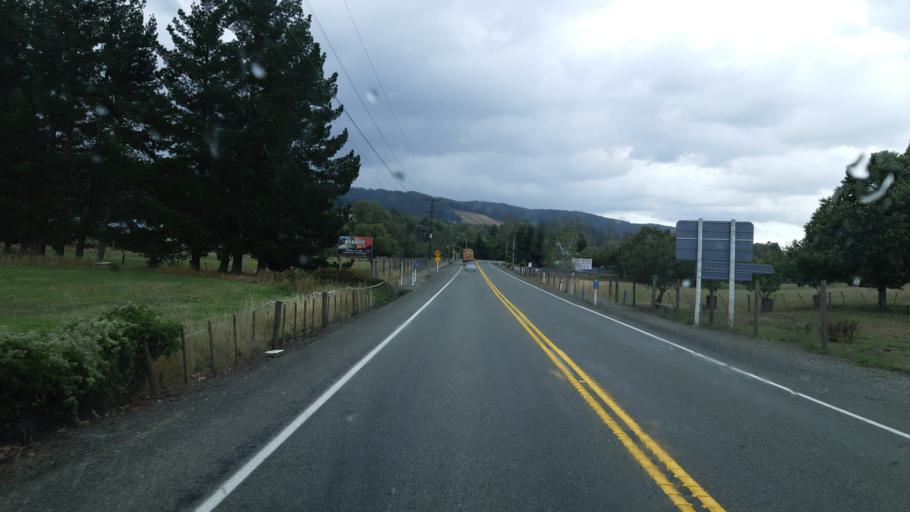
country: NZ
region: Tasman
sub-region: Tasman District
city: Wakefield
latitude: -41.4535
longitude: 172.9571
